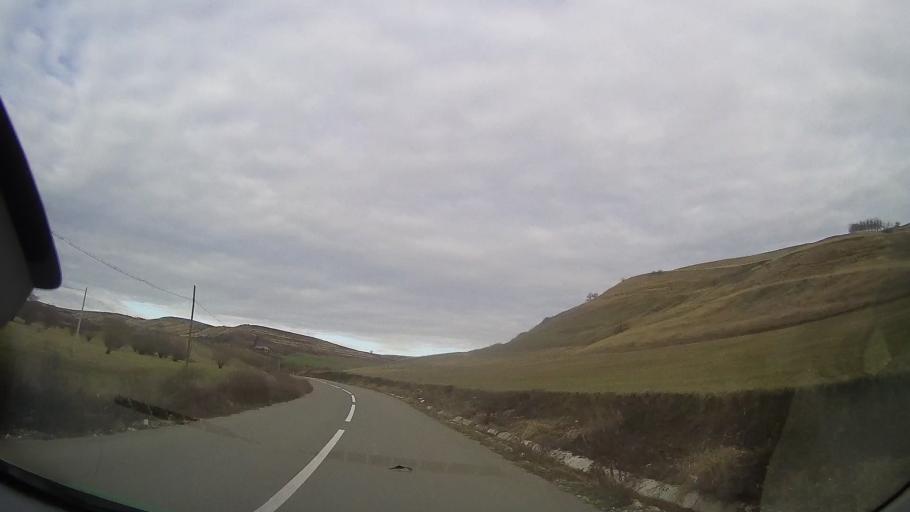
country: RO
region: Bistrita-Nasaud
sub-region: Comuna Silvasu de Campie
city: Silvasu de Campie
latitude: 46.8163
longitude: 24.2974
